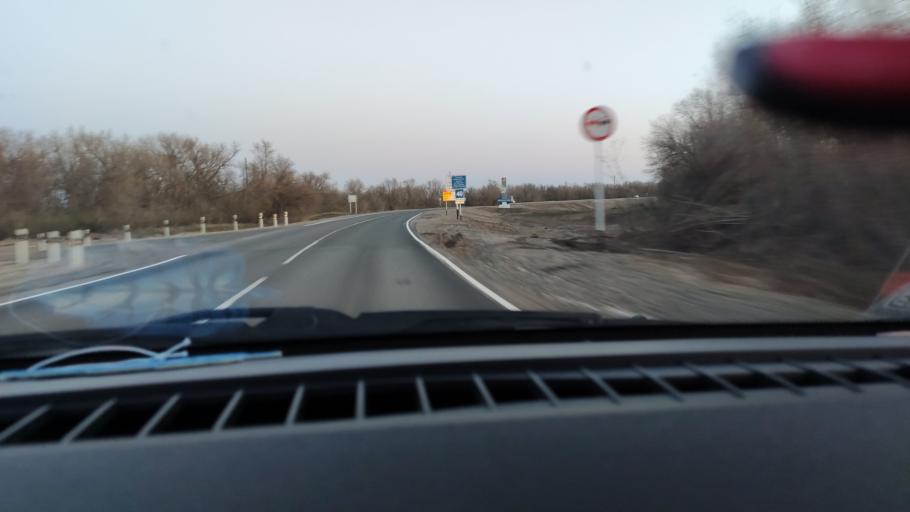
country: RU
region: Saratov
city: Krasnoarmeysk
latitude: 51.1055
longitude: 45.9567
